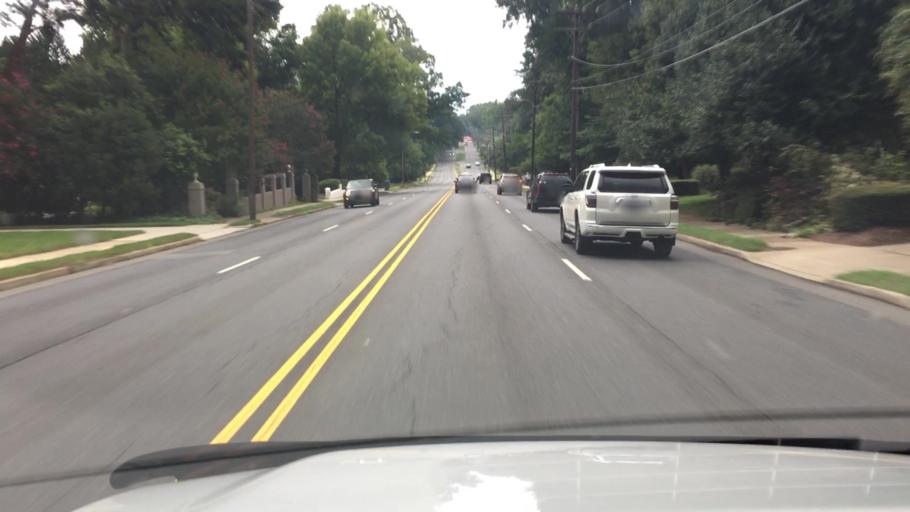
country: US
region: North Carolina
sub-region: Mecklenburg County
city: Charlotte
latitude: 35.1857
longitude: -80.8213
